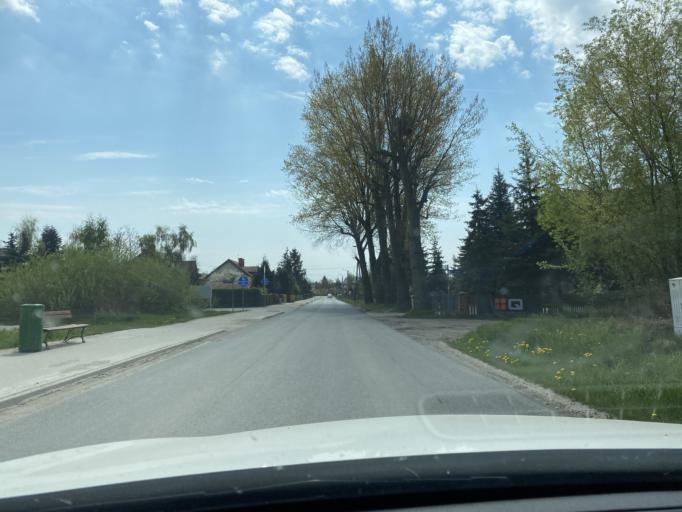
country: PL
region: Lower Silesian Voivodeship
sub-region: Powiat wroclawski
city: Mirkow
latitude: 51.1639
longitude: 17.1651
